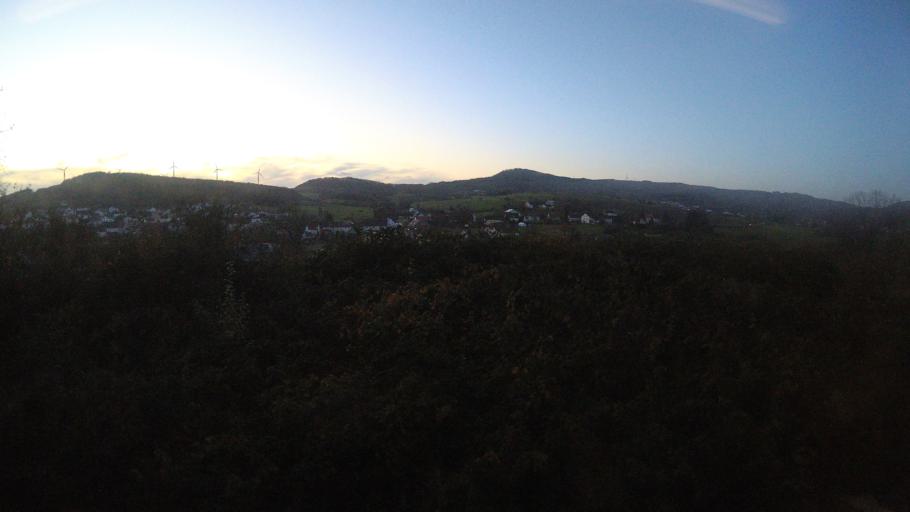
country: DE
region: Rheinland-Pfalz
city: Herchweiler
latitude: 49.5135
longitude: 7.2763
